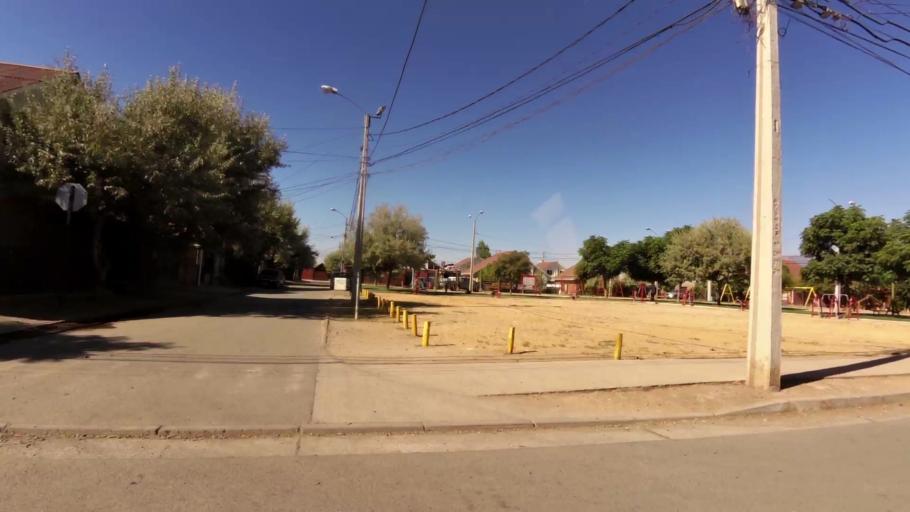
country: CL
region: O'Higgins
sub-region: Provincia de Colchagua
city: Chimbarongo
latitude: -34.5794
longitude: -71.0076
